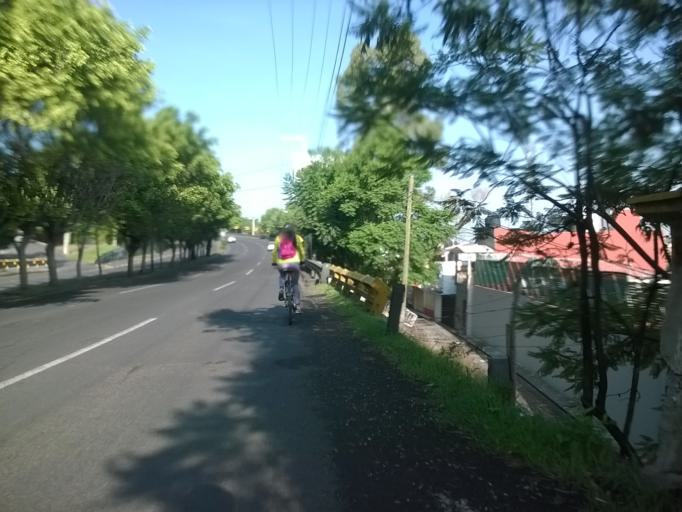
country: MX
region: Michoacan
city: Morelia
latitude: 19.6812
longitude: -101.1989
